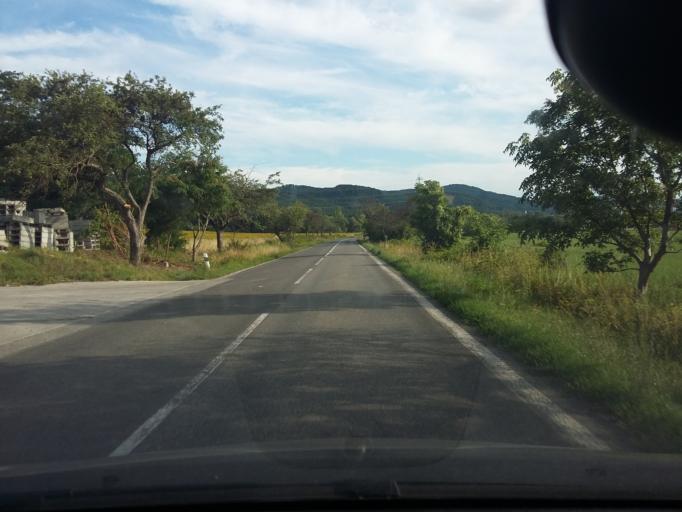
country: SK
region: Bratislavsky
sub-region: Okres Malacky
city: Malacky
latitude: 48.3999
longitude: 17.1550
